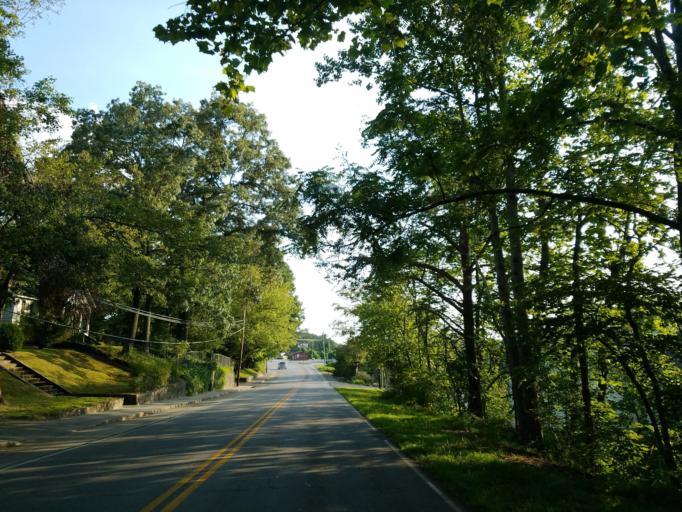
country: US
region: Georgia
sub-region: Fannin County
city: Blue Ridge
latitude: 34.8601
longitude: -84.3280
